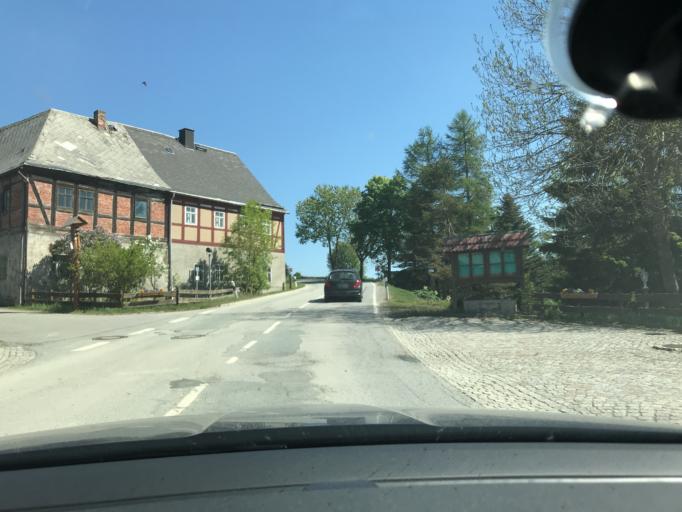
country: CZ
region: Ustecky
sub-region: Okres Chomutov
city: Kovarska
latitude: 50.4450
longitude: 13.0142
